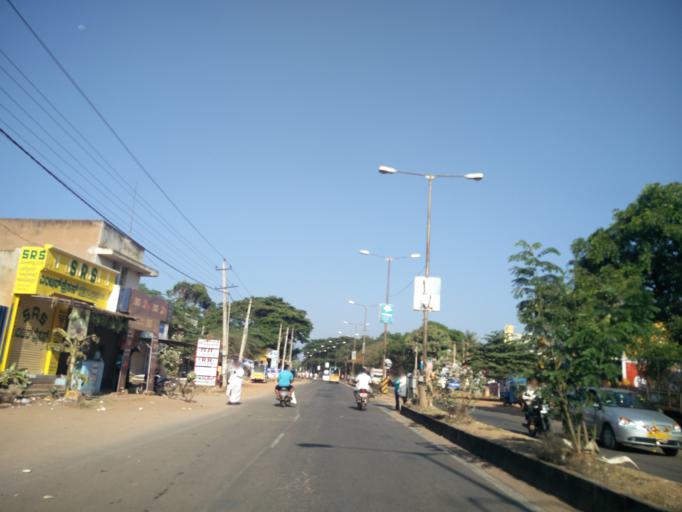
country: IN
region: Karnataka
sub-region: Tumkur
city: Gubbi
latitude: 13.3091
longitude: 76.9396
